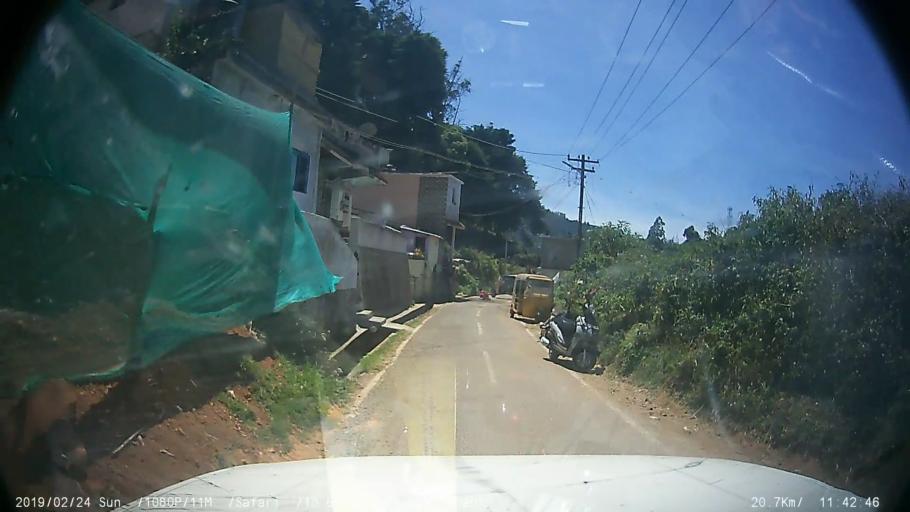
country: IN
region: Tamil Nadu
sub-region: Nilgiri
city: Ooty
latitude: 11.4206
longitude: 76.7062
